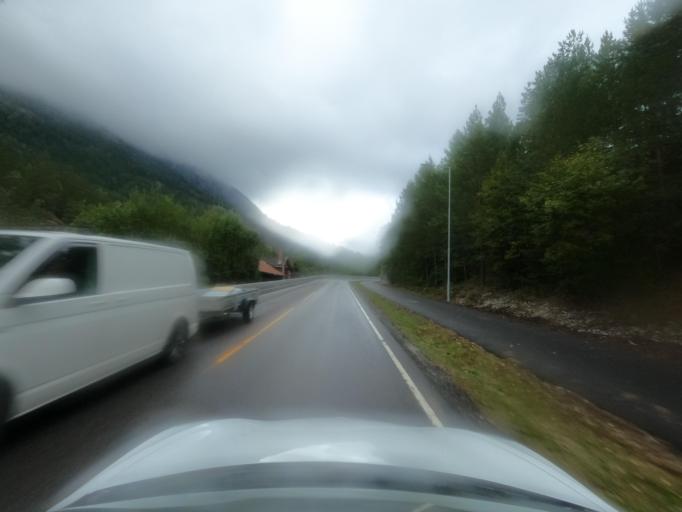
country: NO
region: Telemark
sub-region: Seljord
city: Seljord
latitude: 59.4990
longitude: 8.6365
